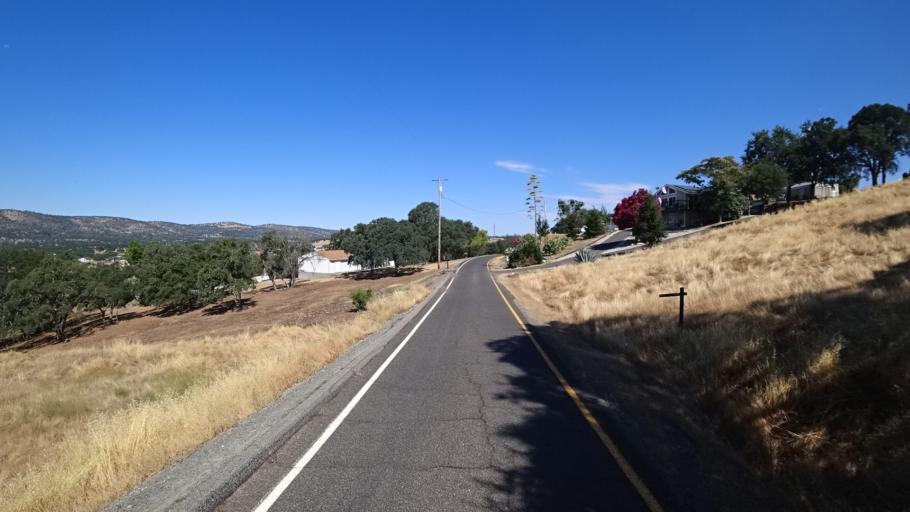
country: US
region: California
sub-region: Calaveras County
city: Copperopolis
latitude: 37.9310
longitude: -120.6363
